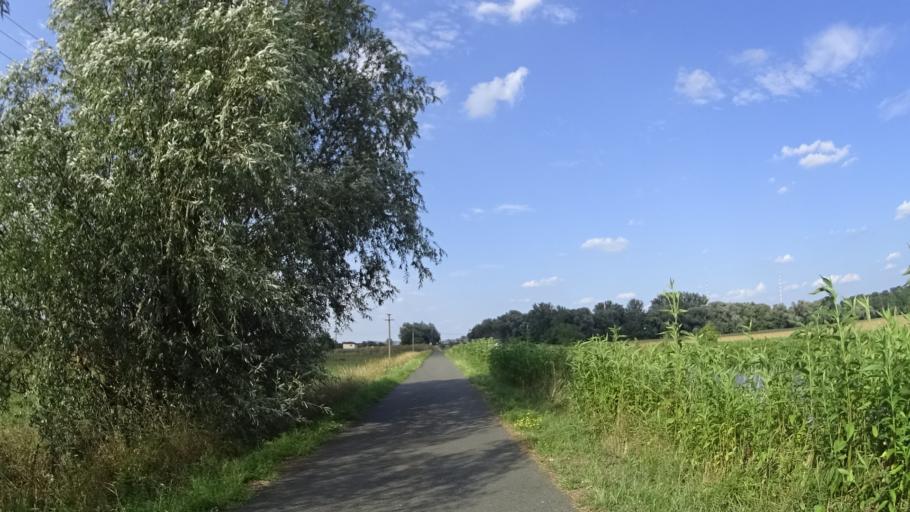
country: CZ
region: Zlin
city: Babice
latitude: 49.1137
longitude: 17.4818
